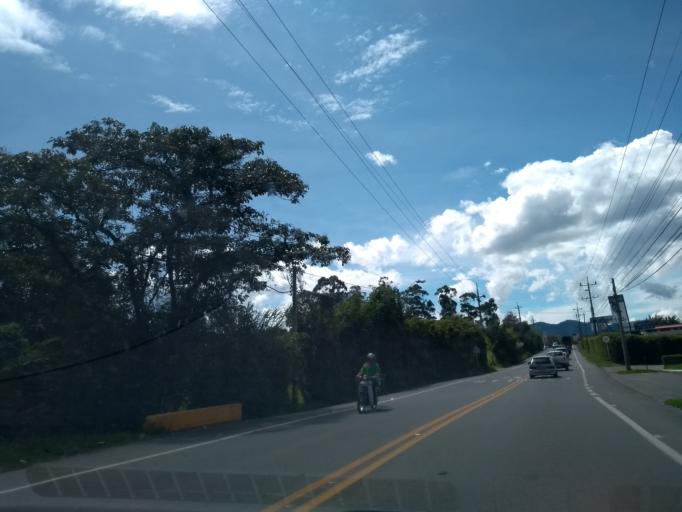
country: CO
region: Antioquia
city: La Ceja
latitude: 6.0488
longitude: -75.3941
